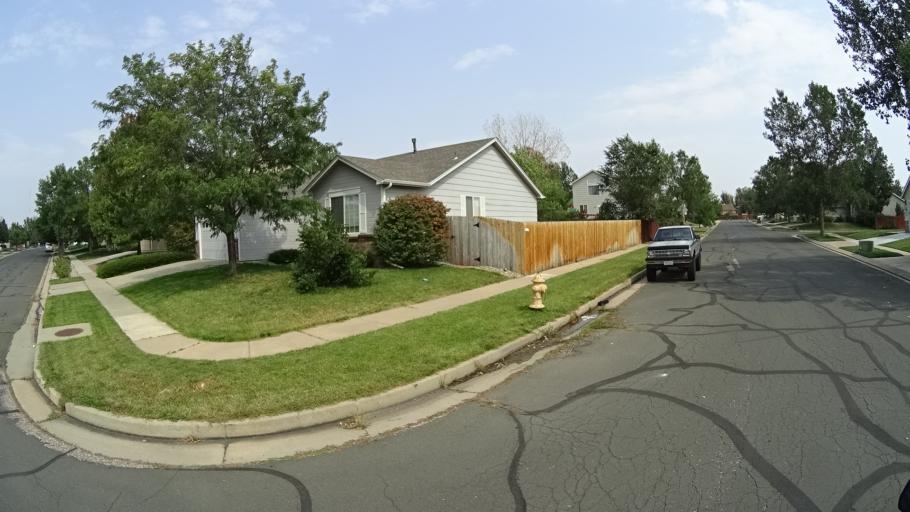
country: US
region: Colorado
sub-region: El Paso County
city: Cimarron Hills
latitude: 38.8212
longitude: -104.7423
